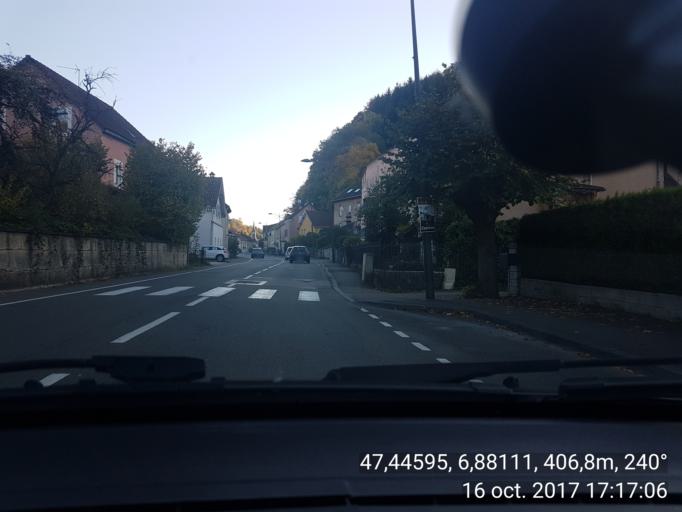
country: FR
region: Franche-Comte
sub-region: Departement du Doubs
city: Herimoncourt
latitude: 47.4458
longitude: 6.8811
